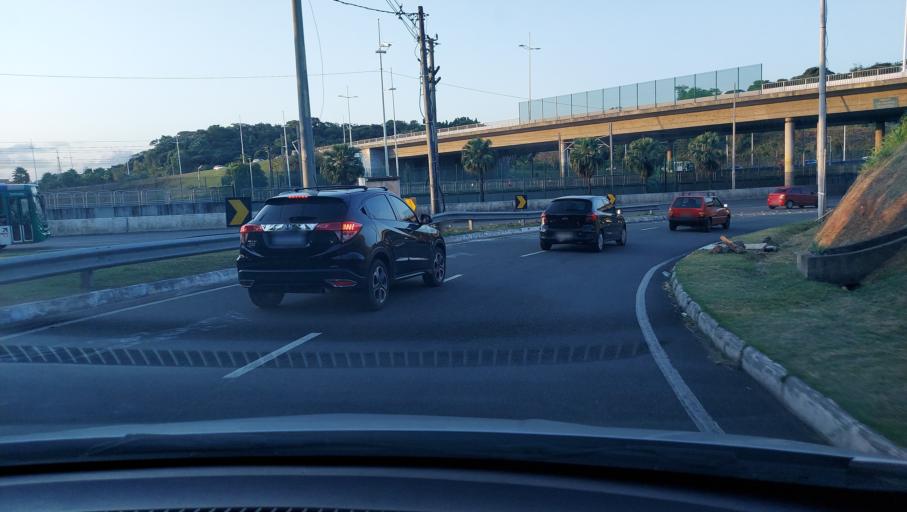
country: BR
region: Bahia
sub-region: Salvador
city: Salvador
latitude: -12.9745
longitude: -38.4500
